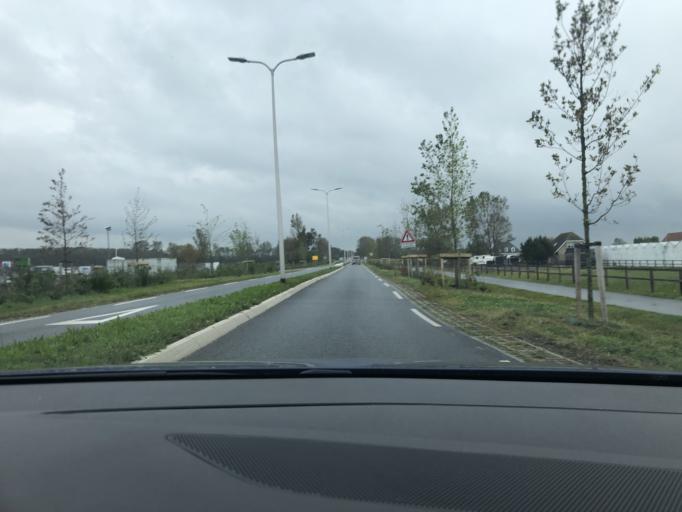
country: NL
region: South Holland
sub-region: Gemeente Noordwijk
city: Noordwijk-Binnen
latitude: 52.2262
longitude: 4.4474
